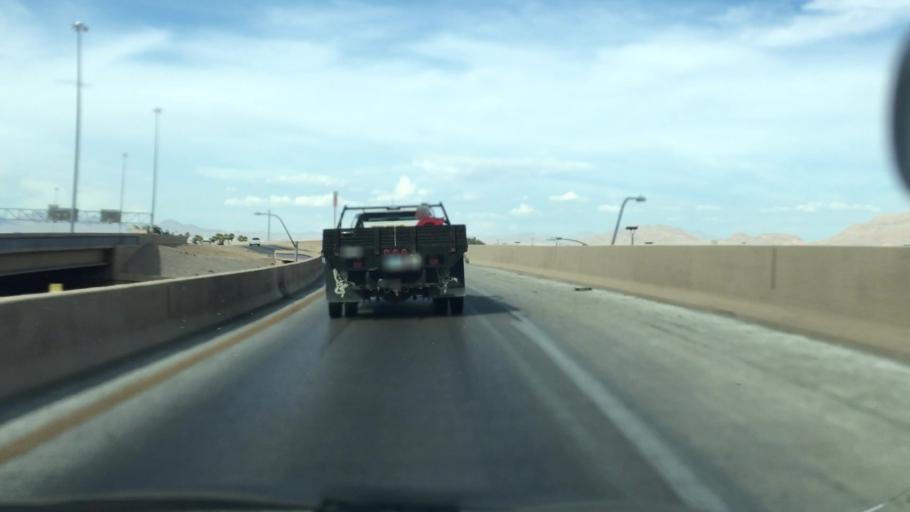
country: US
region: Nevada
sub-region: Clark County
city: Las Vegas
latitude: 36.1789
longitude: -115.1473
